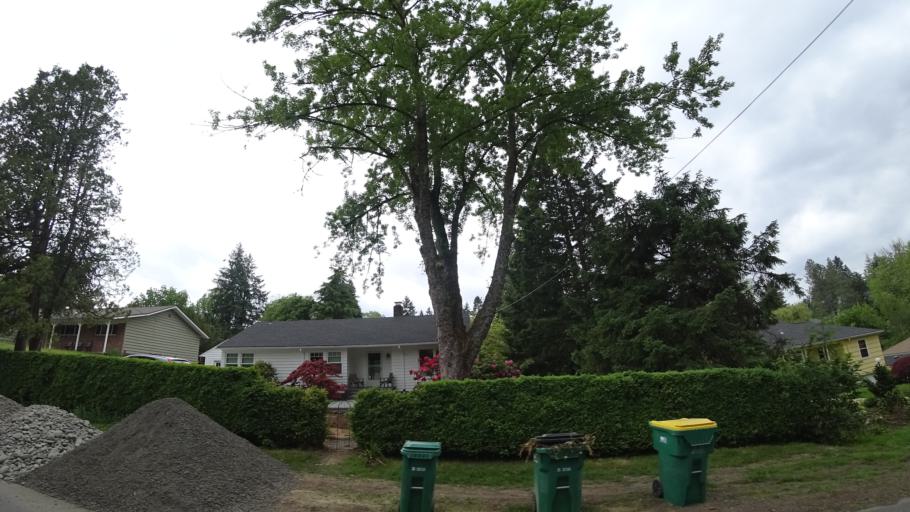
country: US
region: Oregon
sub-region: Washington County
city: West Slope
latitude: 45.4919
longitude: -122.7769
